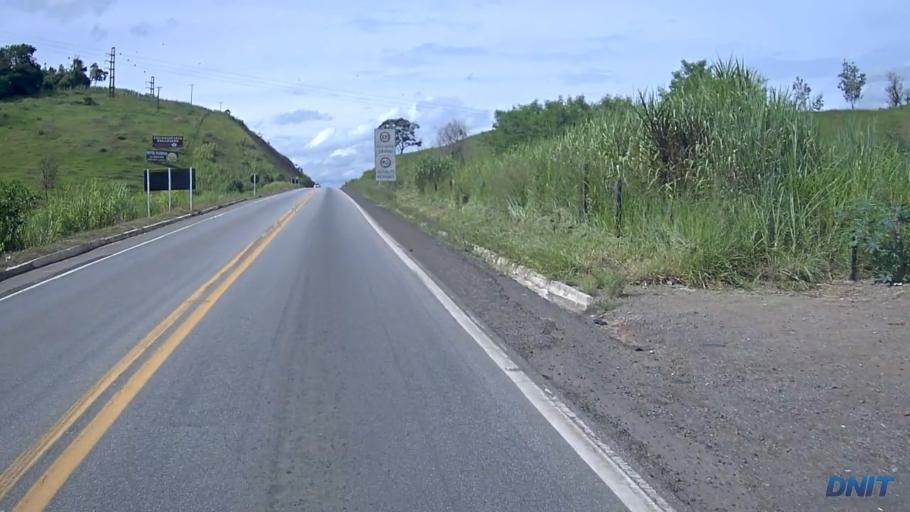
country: BR
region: Minas Gerais
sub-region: Ipatinga
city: Ipatinga
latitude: -19.4176
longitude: -42.4929
